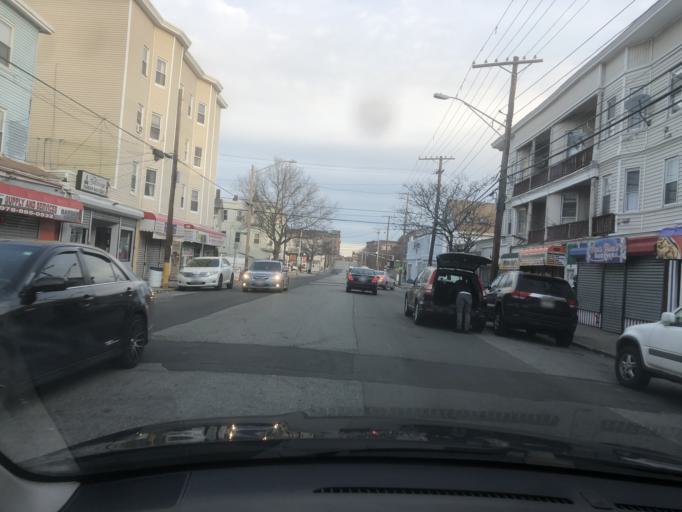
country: US
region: Massachusetts
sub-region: Essex County
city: Lawrence
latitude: 42.6980
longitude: -71.1534
